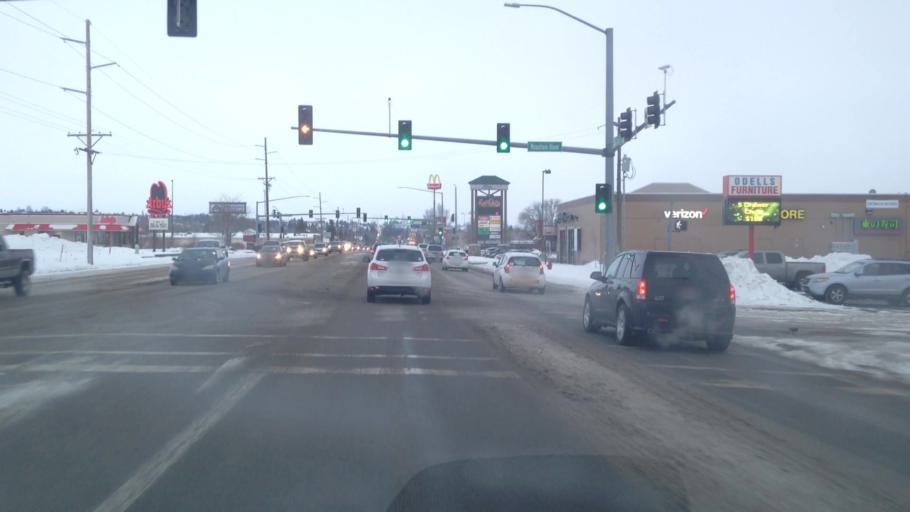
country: US
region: Idaho
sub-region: Madison County
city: Rexburg
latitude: 43.8374
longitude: -111.7781
